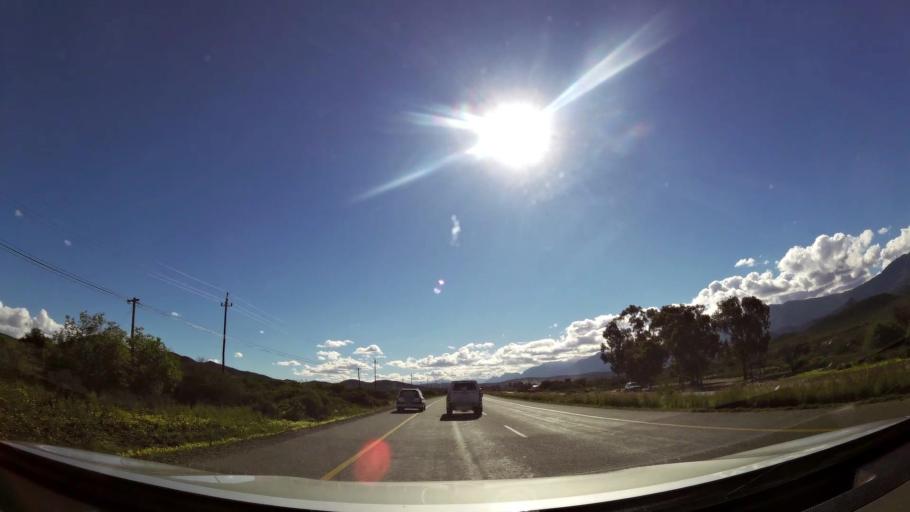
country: ZA
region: Western Cape
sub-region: Cape Winelands District Municipality
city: Ashton
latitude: -33.7738
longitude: 19.7540
